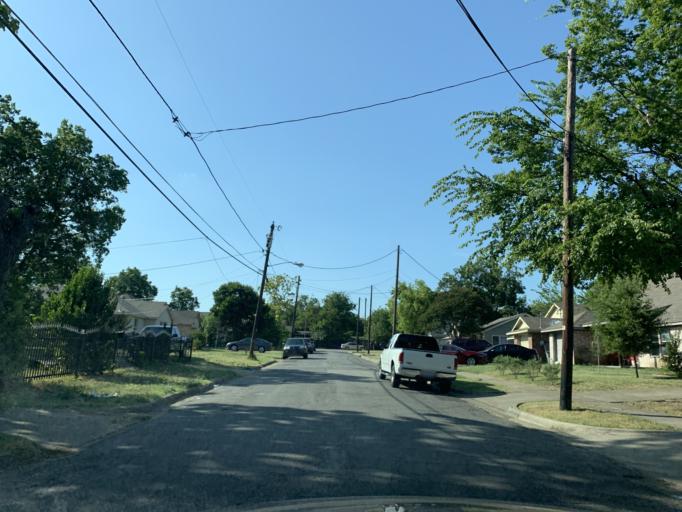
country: US
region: Texas
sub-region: Dallas County
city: Dallas
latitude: 32.6996
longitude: -96.7944
